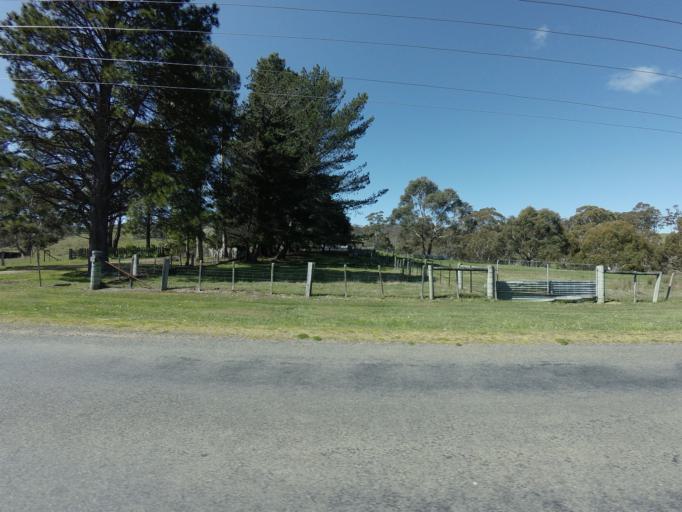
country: AU
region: Tasmania
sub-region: Derwent Valley
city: New Norfolk
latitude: -42.6223
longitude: 146.7209
